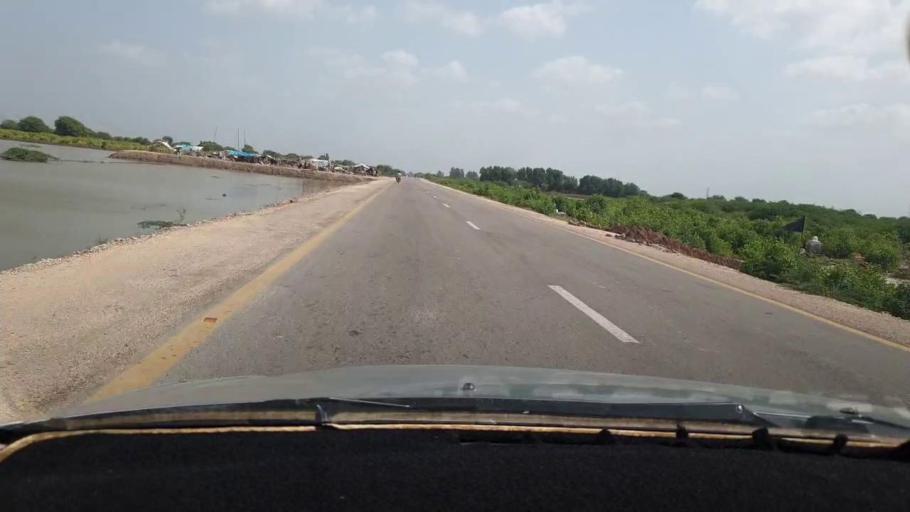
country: PK
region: Sindh
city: Digri
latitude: 25.1148
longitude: 69.1569
